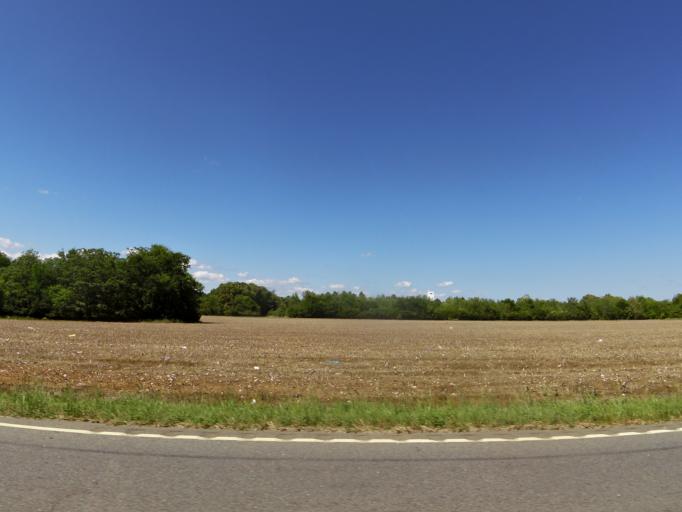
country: US
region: South Carolina
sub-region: Aiken County
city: Aiken
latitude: 33.5383
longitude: -81.6563
